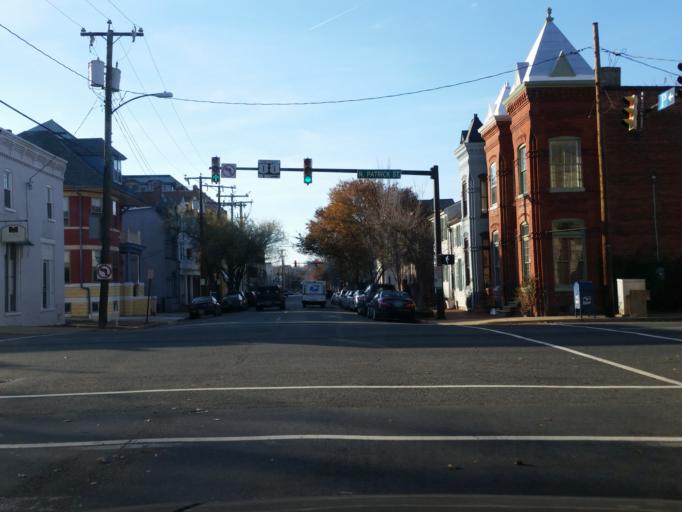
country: US
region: Virginia
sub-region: City of Alexandria
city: Alexandria
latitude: 38.8067
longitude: -77.0499
